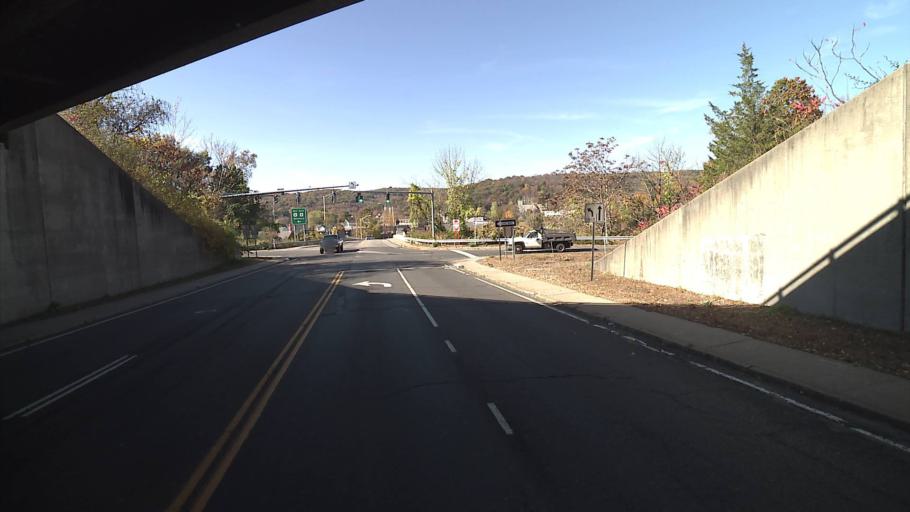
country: US
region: Connecticut
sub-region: Litchfield County
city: Thomaston
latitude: 41.6741
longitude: -73.0665
